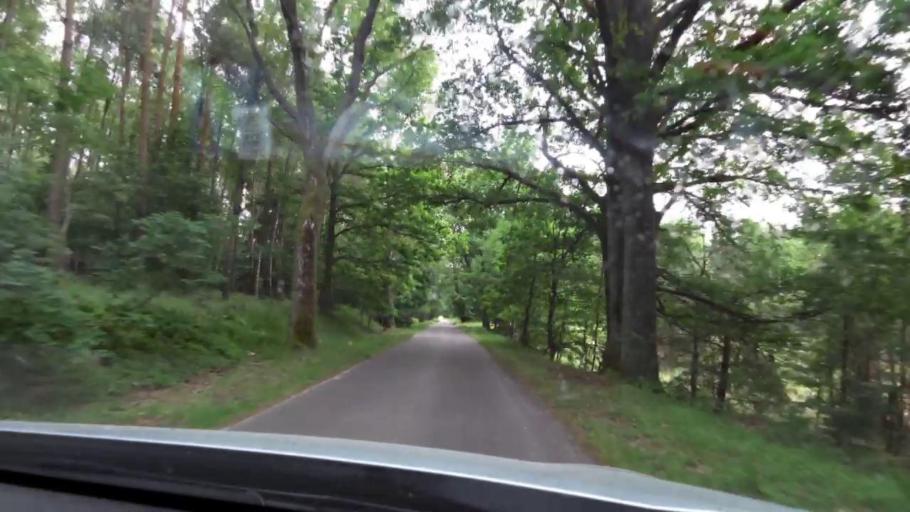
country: PL
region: Pomeranian Voivodeship
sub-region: Powiat bytowski
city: Trzebielino
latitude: 54.2429
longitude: 17.0000
